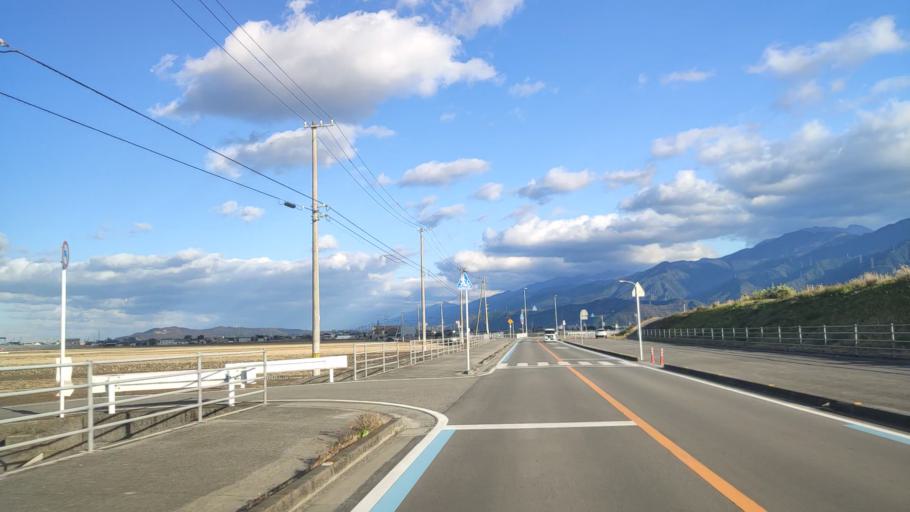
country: JP
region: Ehime
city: Saijo
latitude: 33.9094
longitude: 133.1394
